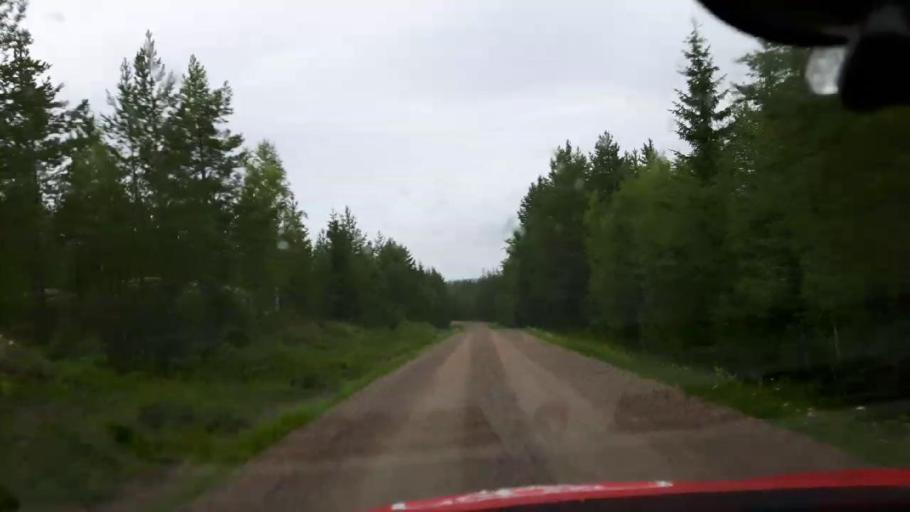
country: SE
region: Jaemtland
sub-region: OEstersunds Kommun
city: Brunflo
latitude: 62.8056
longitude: 14.8977
